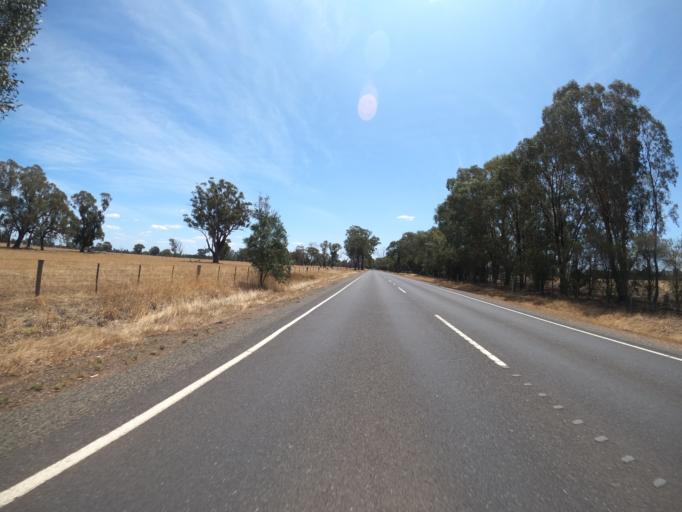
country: AU
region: Victoria
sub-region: Benalla
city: Benalla
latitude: -36.5085
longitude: 146.0271
